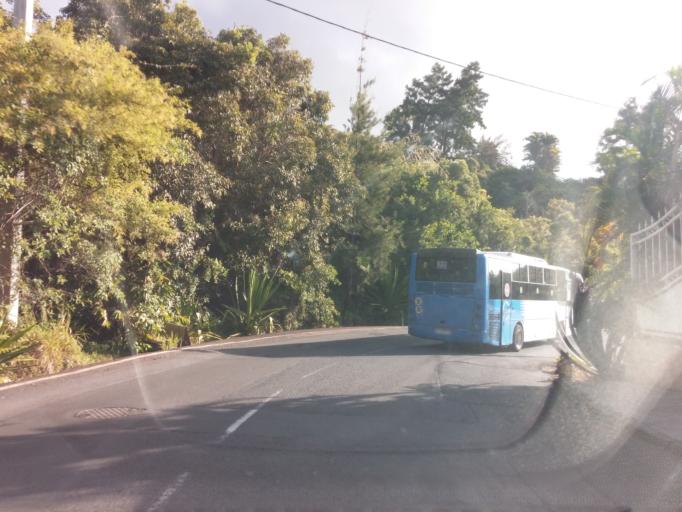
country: RE
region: Reunion
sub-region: Reunion
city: Saint-Denis
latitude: -20.8872
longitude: 55.4193
